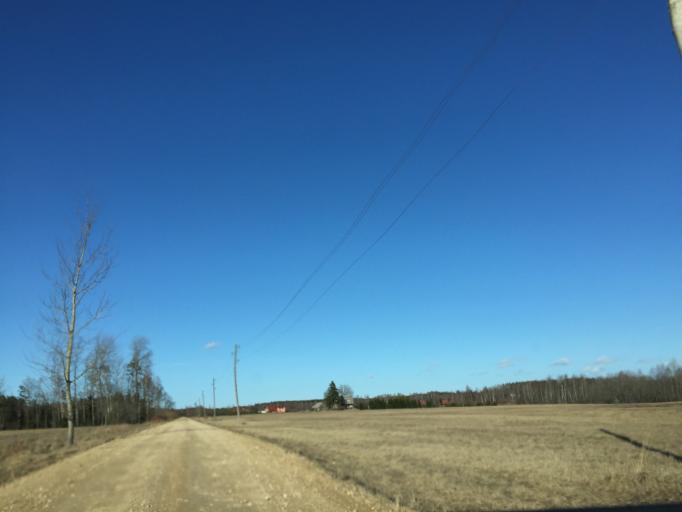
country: LV
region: Ogre
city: Ogre
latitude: 56.8709
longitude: 24.7067
